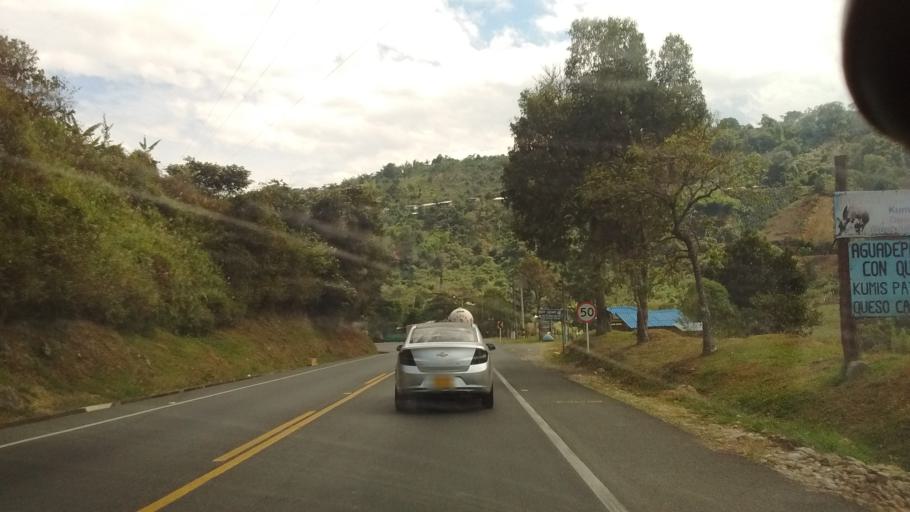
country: CO
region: Cauca
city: Cajibio
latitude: 2.6229
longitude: -76.5196
